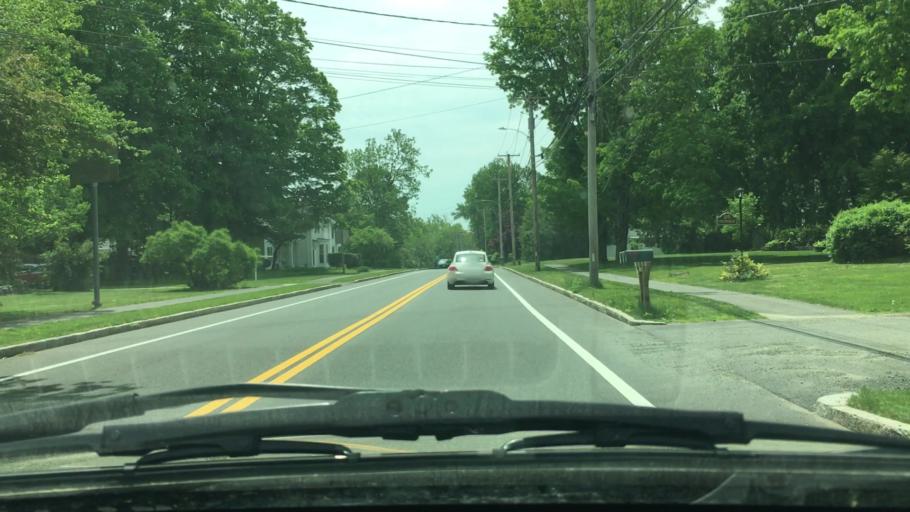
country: US
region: Massachusetts
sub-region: Hampshire County
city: Belchertown
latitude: 42.2758
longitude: -72.4001
